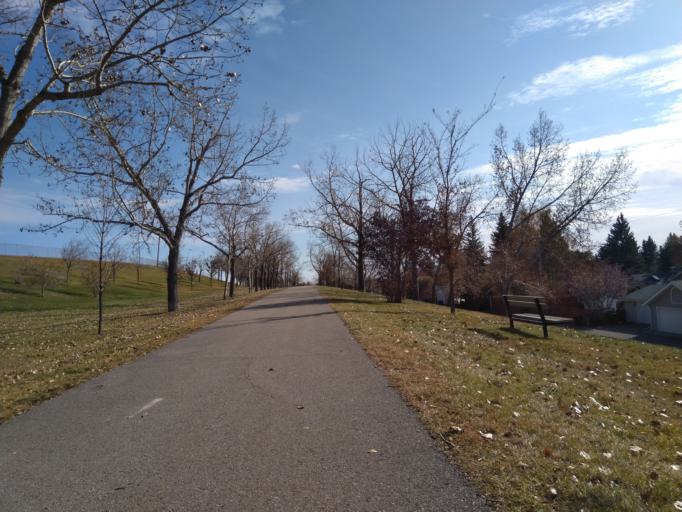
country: CA
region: Alberta
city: Calgary
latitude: 51.0953
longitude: -114.1153
